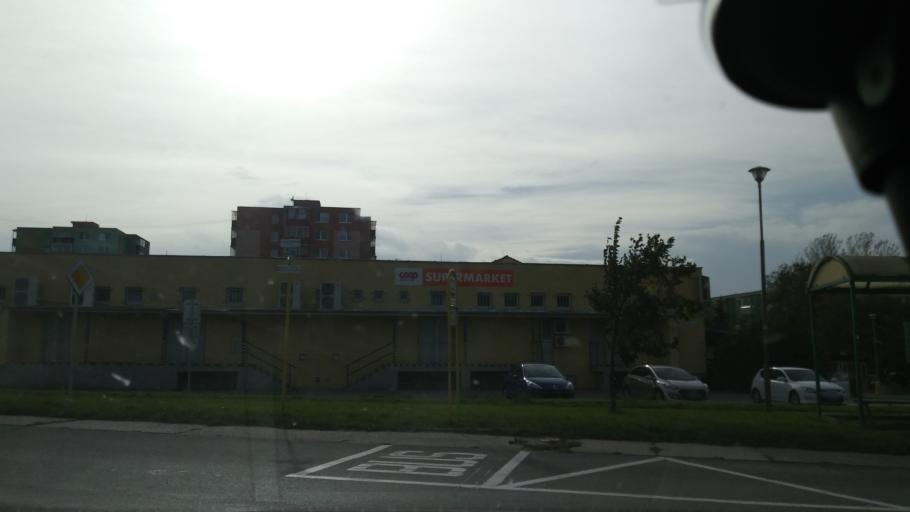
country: SK
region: Trnavsky
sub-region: Okres Skalica
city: Skalica
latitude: 48.8391
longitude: 17.2307
